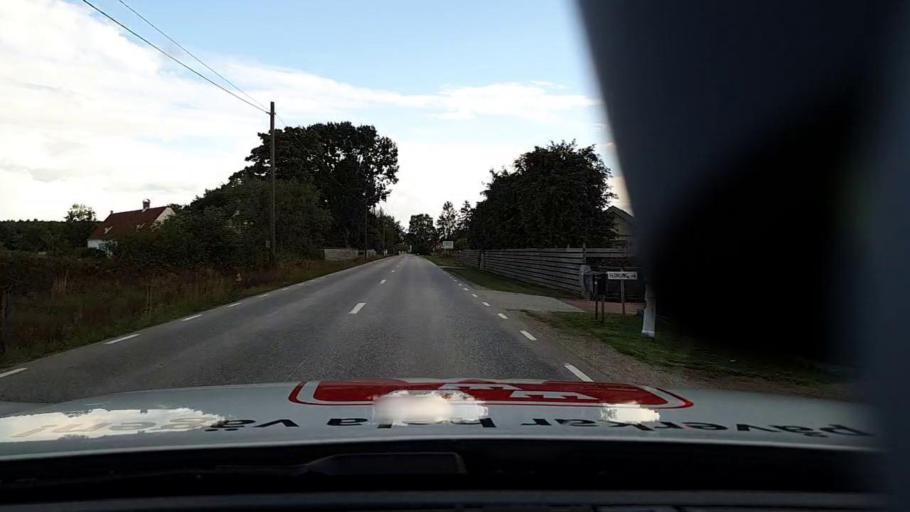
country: SE
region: Blekinge
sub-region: Solvesborgs Kommun
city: Soelvesborg
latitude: 56.0197
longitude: 14.7165
